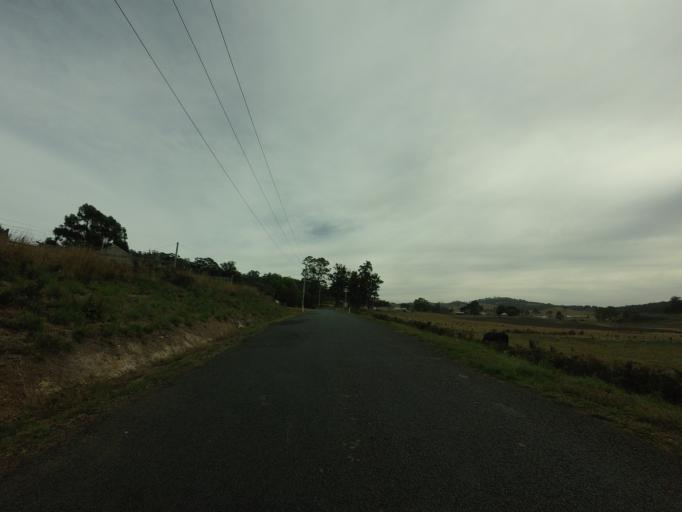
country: AU
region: Tasmania
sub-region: Sorell
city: Sorell
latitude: -42.4685
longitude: 147.5681
